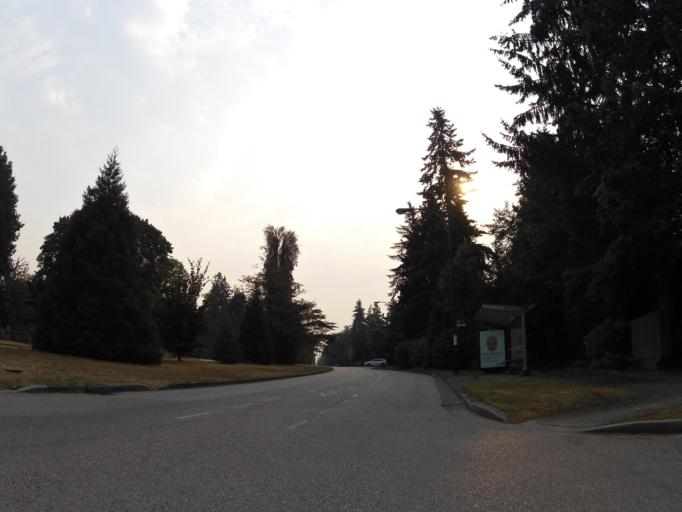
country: CA
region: British Columbia
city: Vancouver
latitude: 49.2495
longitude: -123.1489
